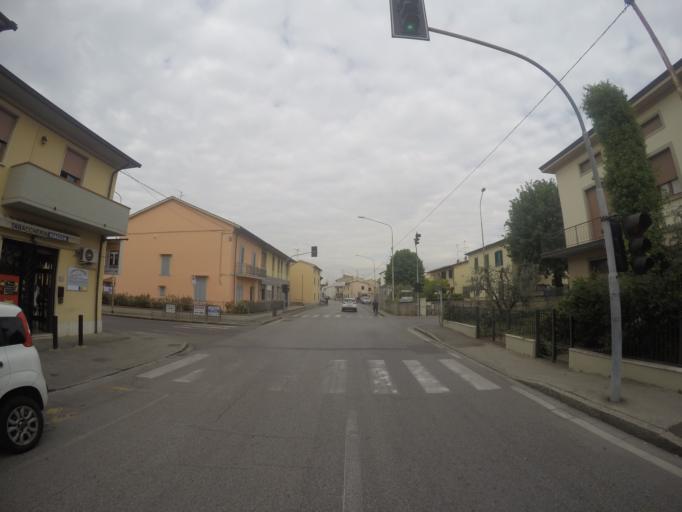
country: IT
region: Tuscany
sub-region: Provincia di Prato
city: Fornacelle
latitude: 43.8979
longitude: 11.0563
